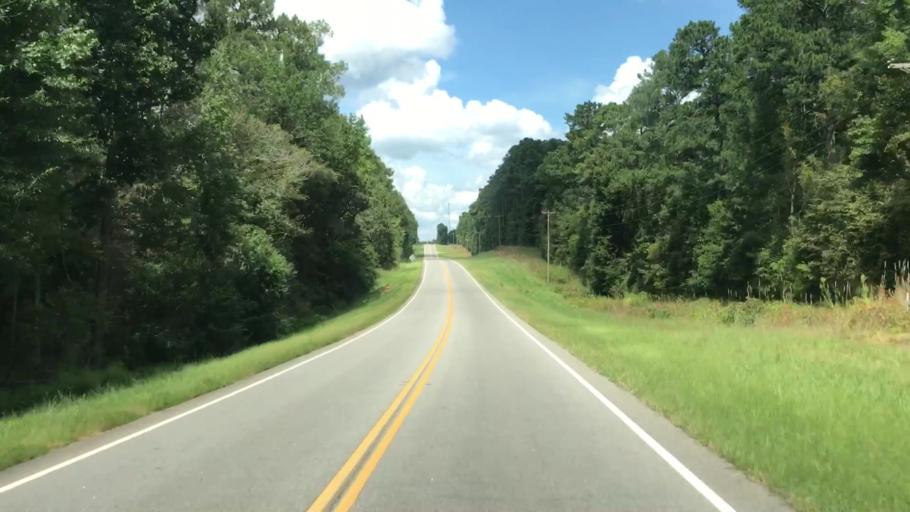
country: US
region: Georgia
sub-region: Greene County
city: Greensboro
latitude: 33.6546
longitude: -83.2374
